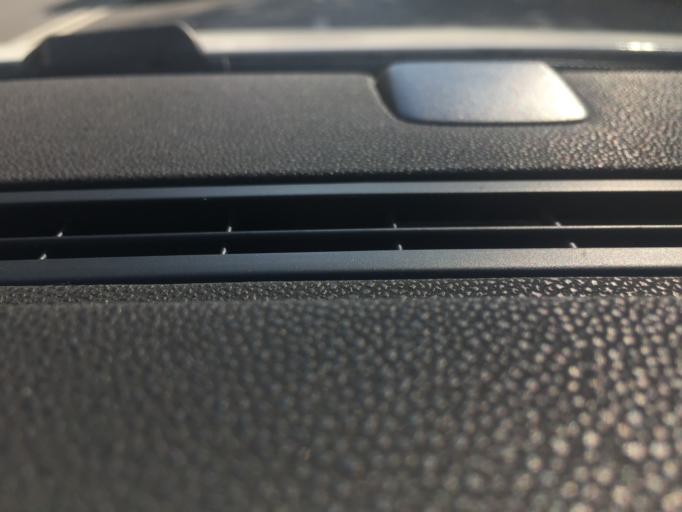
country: KZ
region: Almaty Qalasy
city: Almaty
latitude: 43.2472
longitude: 76.9030
